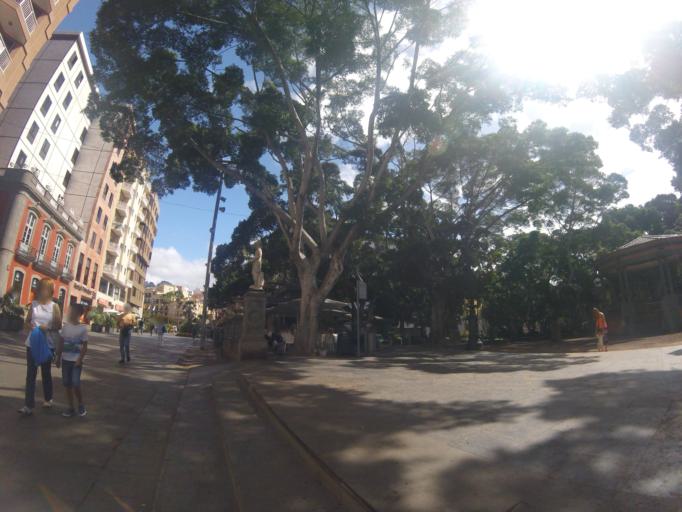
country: ES
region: Canary Islands
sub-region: Provincia de Santa Cruz de Tenerife
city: Santa Cruz de Tenerife
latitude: 28.4683
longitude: -16.2507
